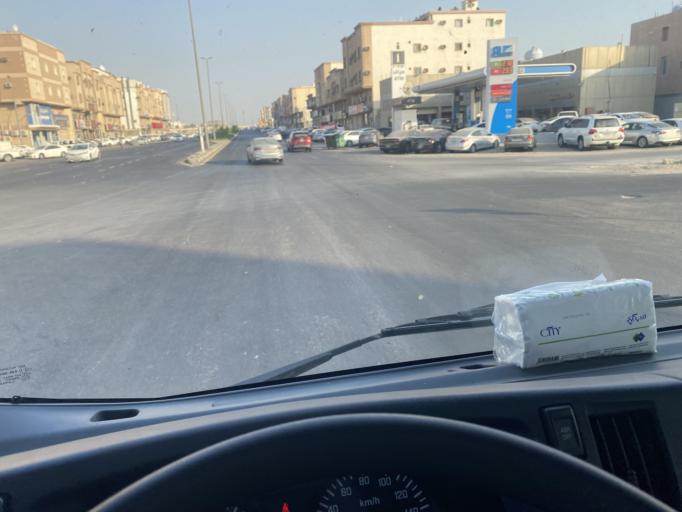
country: SA
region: Eastern Province
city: Dhahran
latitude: 26.3547
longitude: 50.0477
